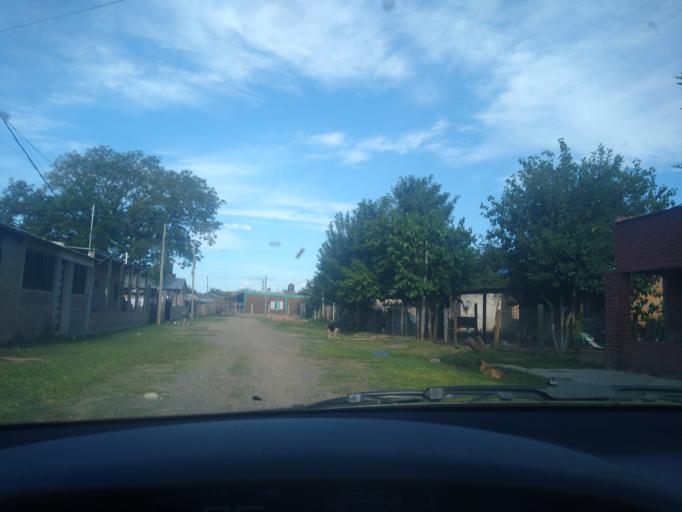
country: AR
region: Chaco
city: Barranqueras
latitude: -27.4723
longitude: -58.9265
